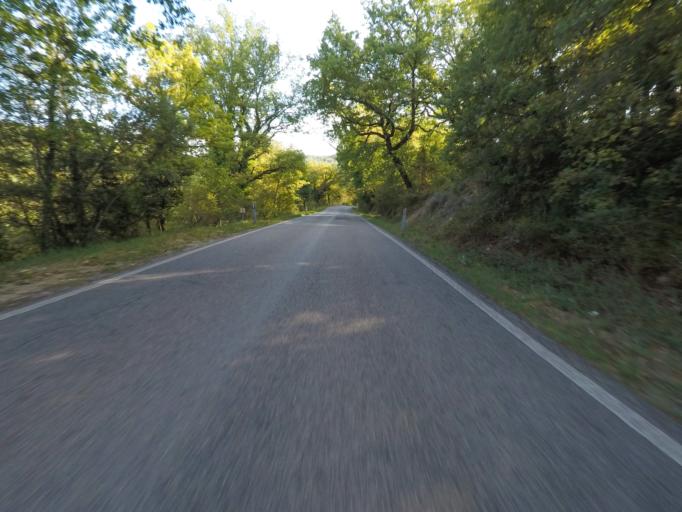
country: IT
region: Tuscany
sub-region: Provincia di Siena
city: Radda in Chianti
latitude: 43.4757
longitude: 11.3738
